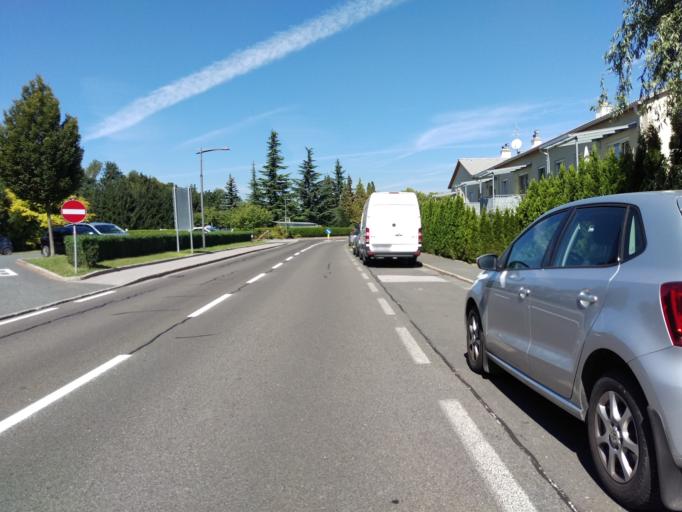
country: AT
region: Styria
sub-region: Politischer Bezirk Graz-Umgebung
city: Nestelbach bei Graz
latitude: 47.0800
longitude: 15.5803
